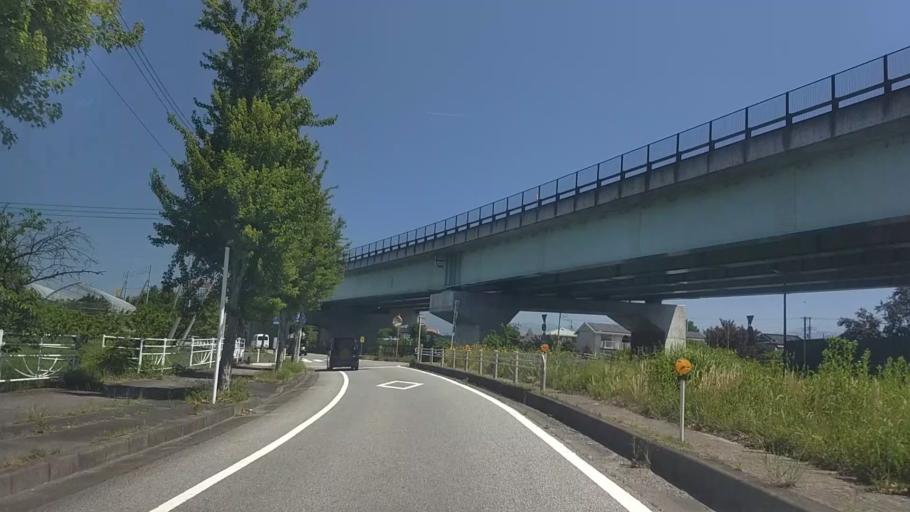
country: JP
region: Yamanashi
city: Ryuo
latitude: 35.6172
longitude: 138.4791
